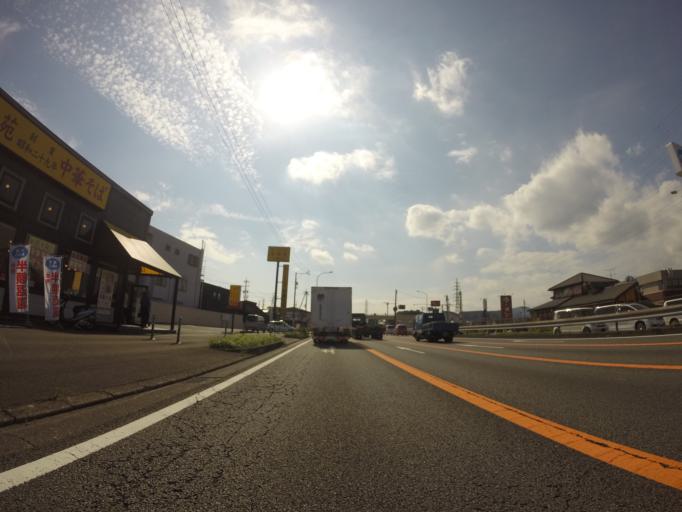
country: JP
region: Shizuoka
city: Shizuoka-shi
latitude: 35.0397
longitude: 138.4817
